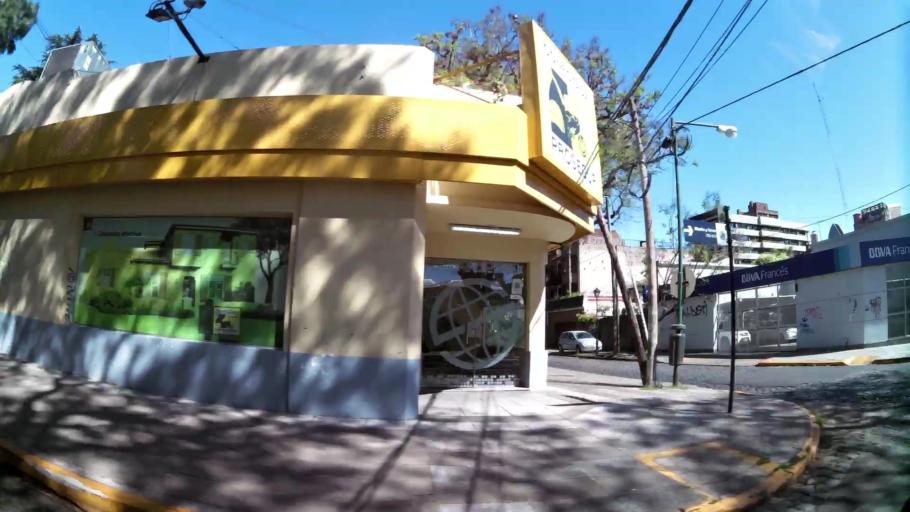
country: AR
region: Buenos Aires
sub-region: Partido de San Isidro
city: San Isidro
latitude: -34.4696
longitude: -58.5082
